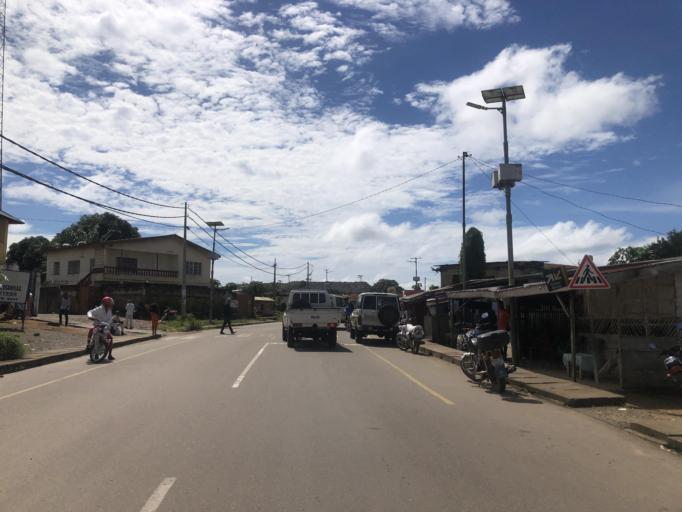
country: SL
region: Eastern Province
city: Koidu
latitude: 8.6393
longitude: -10.9750
